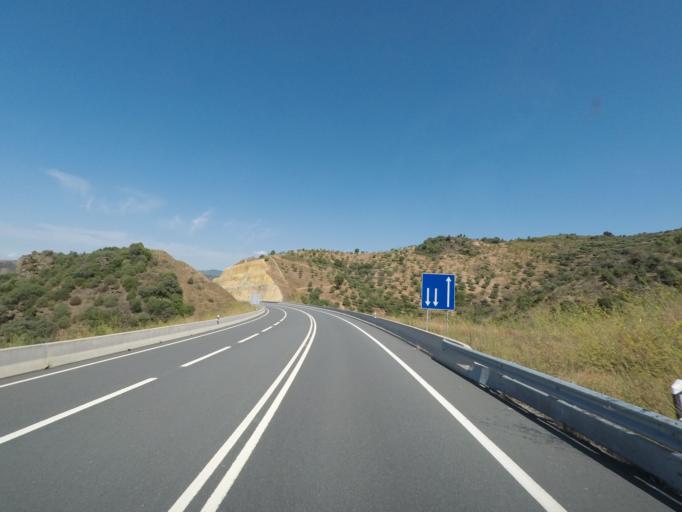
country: PT
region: Braganca
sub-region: Alfandega da Fe
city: Alfandega da Fe
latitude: 41.2942
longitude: -6.8961
